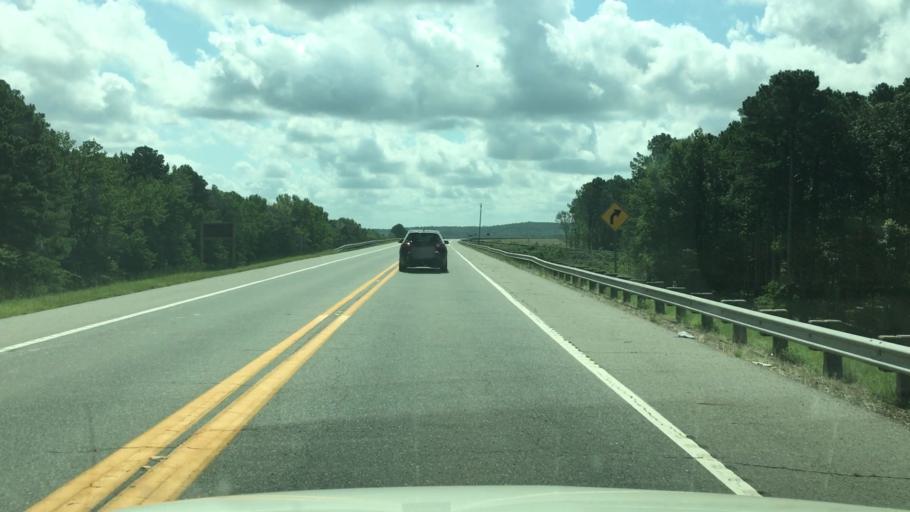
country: US
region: Arkansas
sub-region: Clark County
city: Arkadelphia
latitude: 34.2476
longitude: -93.1134
